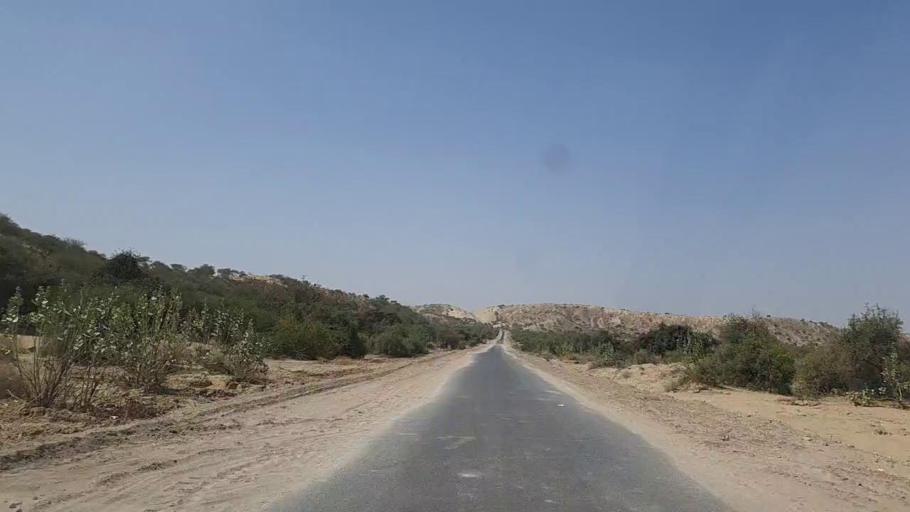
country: PK
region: Sindh
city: Diplo
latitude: 24.5862
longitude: 69.5287
